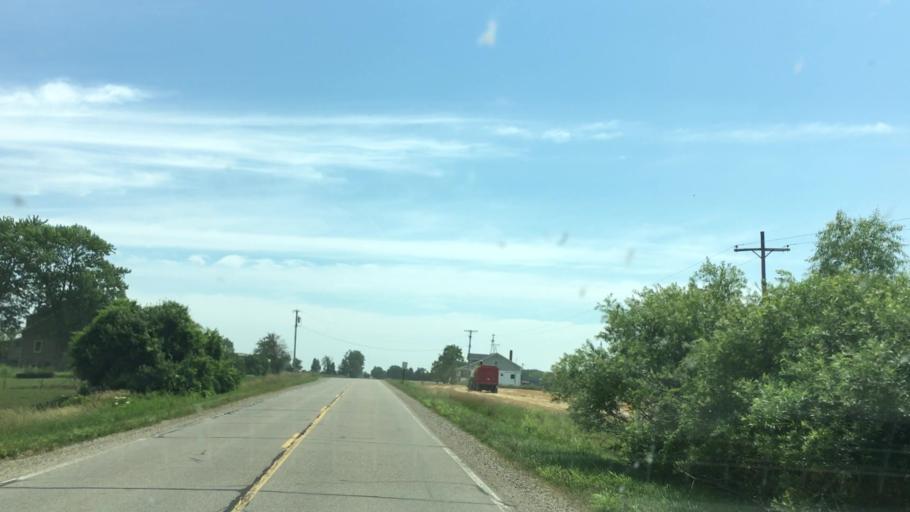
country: US
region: Michigan
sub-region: Sanilac County
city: Marlette
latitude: 43.2552
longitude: -83.0695
